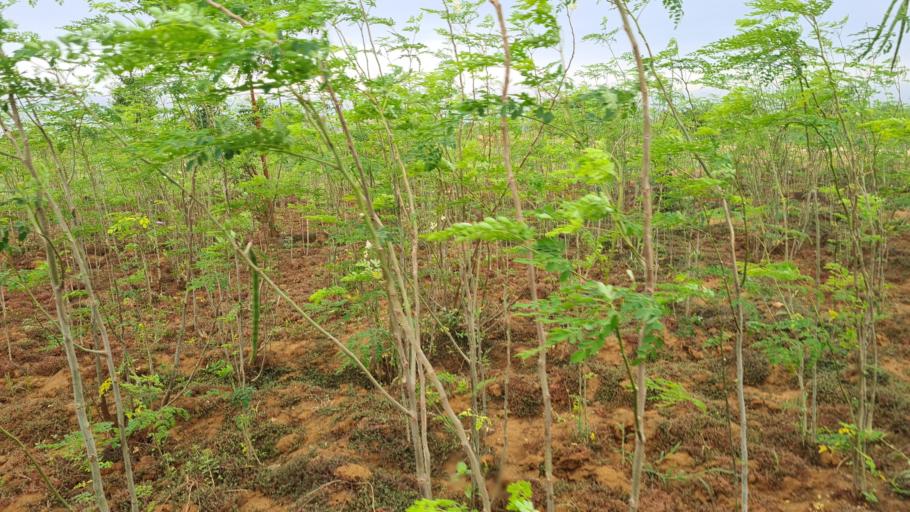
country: NE
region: Tahoua
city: Birni N Konni
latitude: 13.8391
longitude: 5.2696
